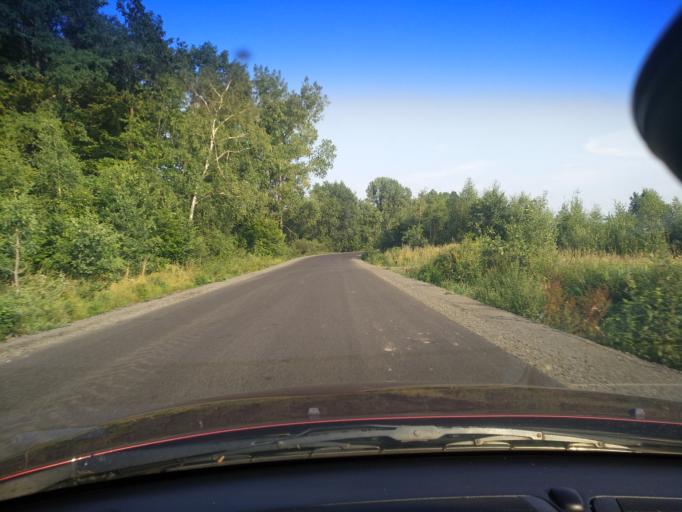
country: PL
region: Lower Silesian Voivodeship
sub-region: Powiat lubanski
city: Siekierczyn
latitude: 51.0535
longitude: 15.1911
